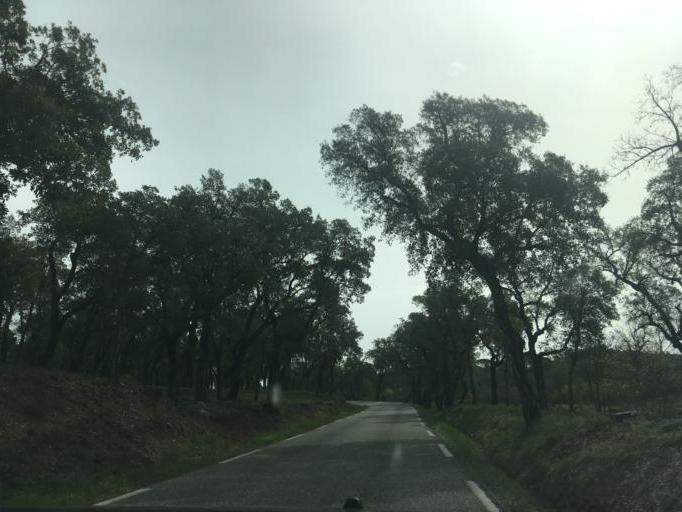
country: FR
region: Provence-Alpes-Cote d'Azur
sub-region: Departement du Var
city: Le Muy
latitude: 43.5143
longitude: 6.6258
